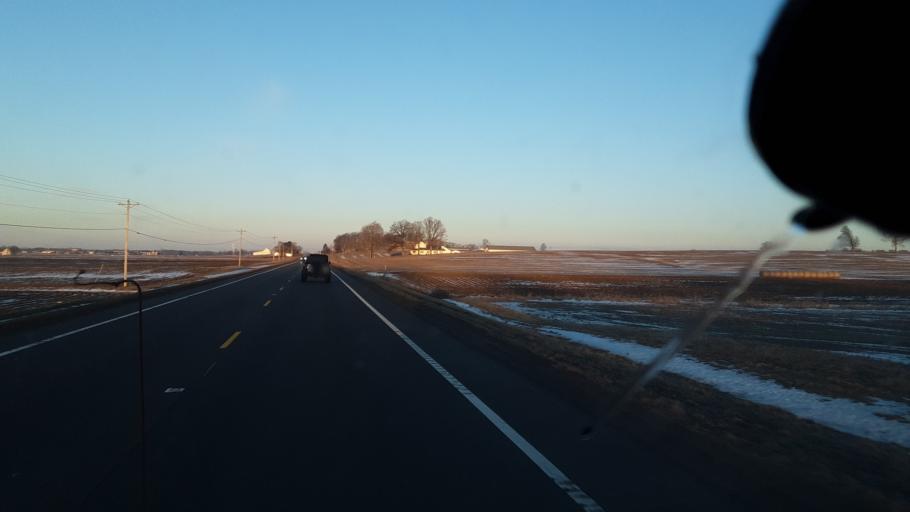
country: US
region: Ohio
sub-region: Perry County
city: Somerset
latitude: 39.8304
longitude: -82.3474
